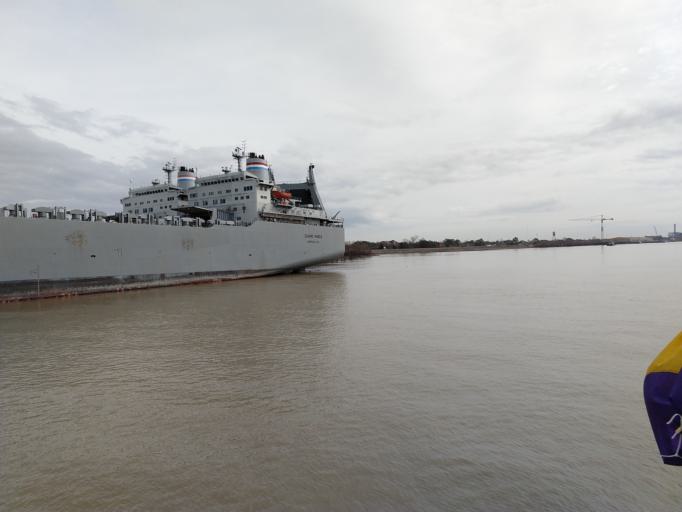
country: US
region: Louisiana
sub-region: Saint Bernard Parish
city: Arabi
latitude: 29.9569
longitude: -90.0336
